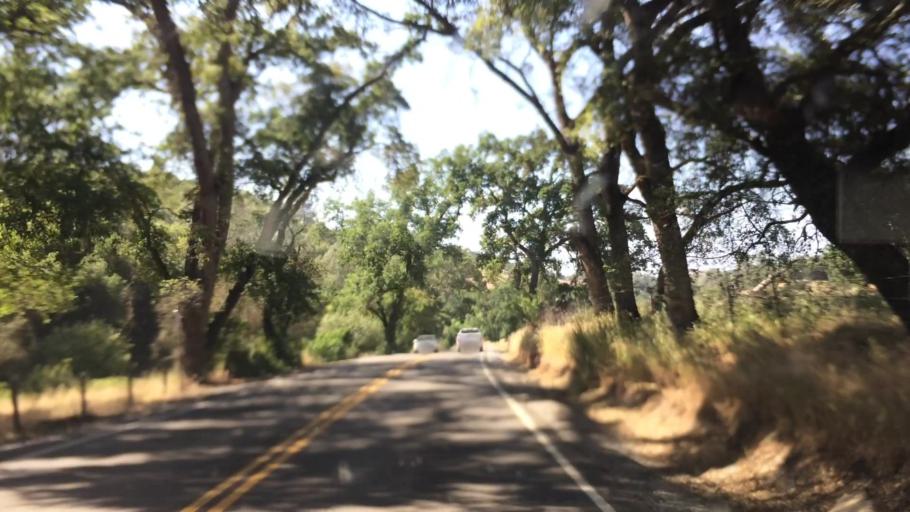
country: US
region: California
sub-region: Amador County
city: Plymouth
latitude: 38.5179
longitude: -120.9525
